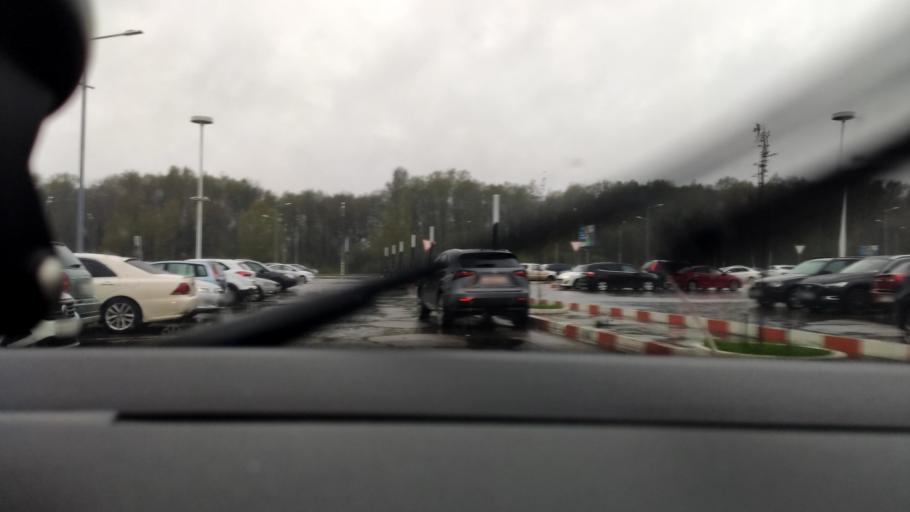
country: RU
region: Moskovskaya
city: Krasnogorsk
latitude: 55.8757
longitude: 37.3308
